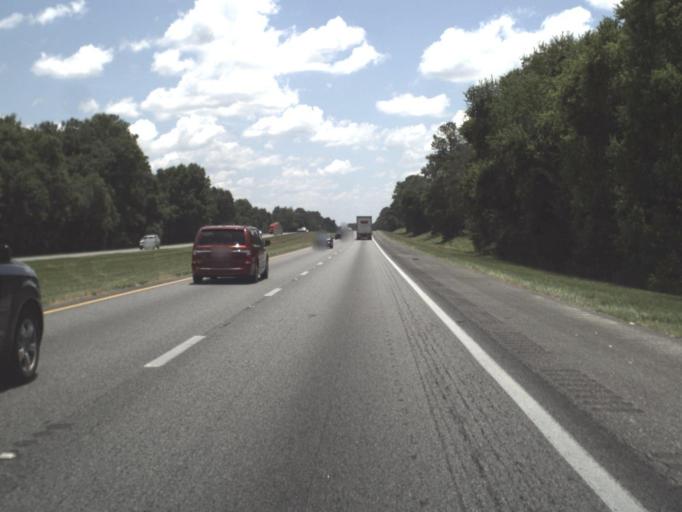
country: US
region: Florida
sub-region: Madison County
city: Madison
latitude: 30.4307
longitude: -83.5851
